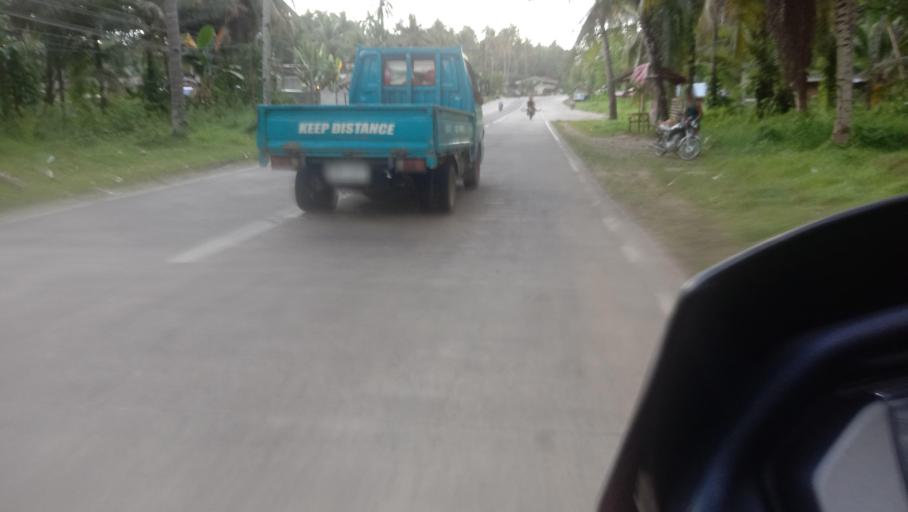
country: PH
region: Caraga
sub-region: Province of Surigao del Sur
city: Barobo
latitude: 8.5174
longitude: 126.1232
